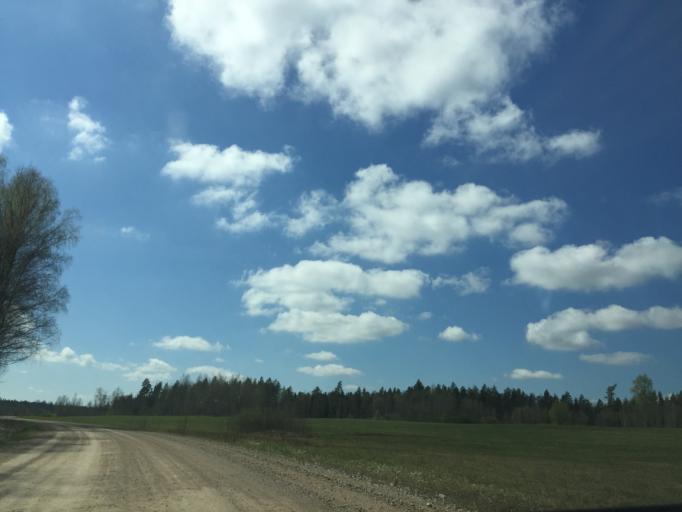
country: LV
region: Valkas Rajons
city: Valka
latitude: 57.5893
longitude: 26.0253
